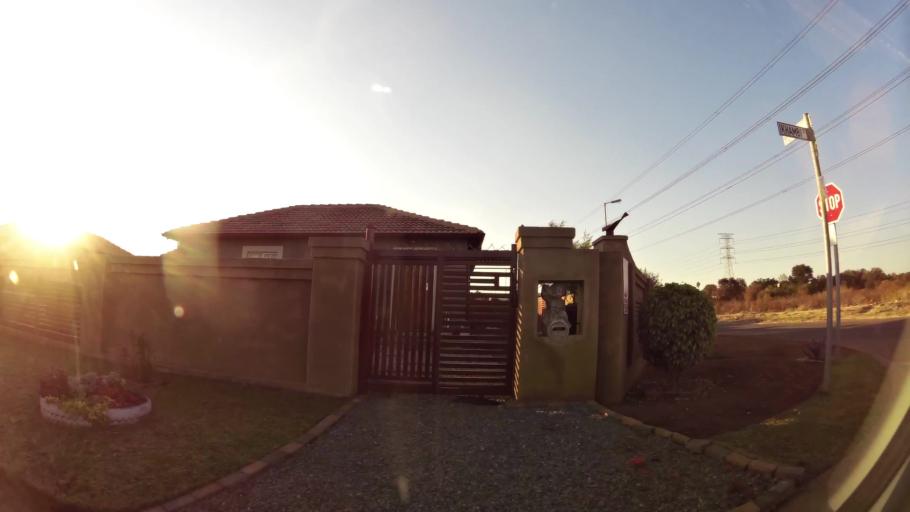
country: ZA
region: Gauteng
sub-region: City of Tshwane Metropolitan Municipality
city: Pretoria
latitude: -25.7444
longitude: 28.1056
